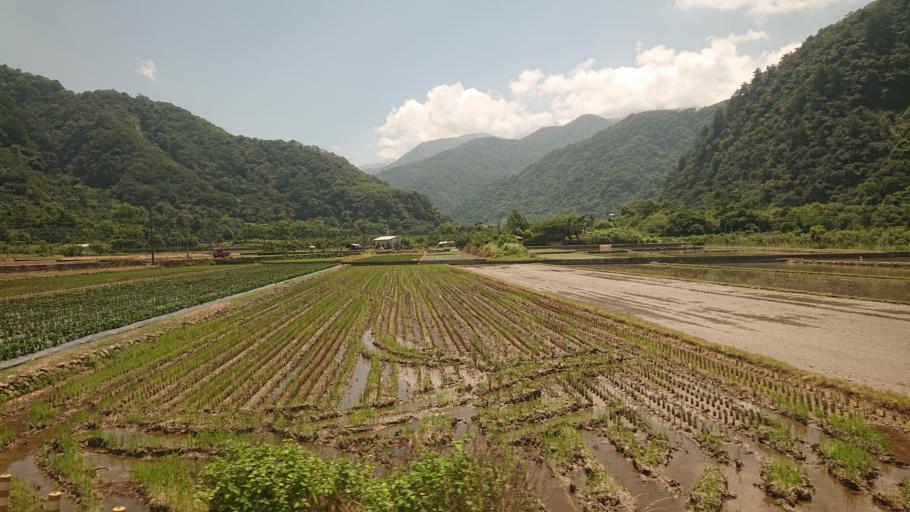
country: TW
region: Taiwan
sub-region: Nantou
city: Puli
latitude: 24.0656
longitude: 120.9531
